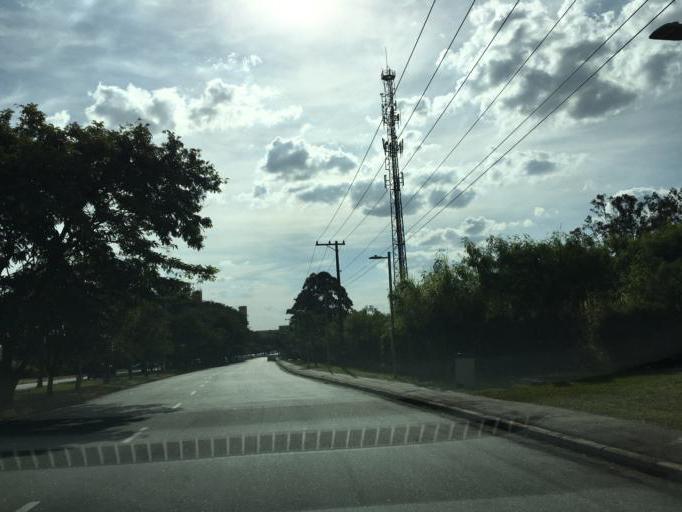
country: BR
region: Sao Paulo
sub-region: Osasco
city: Osasco
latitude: -23.5681
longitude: -46.7357
